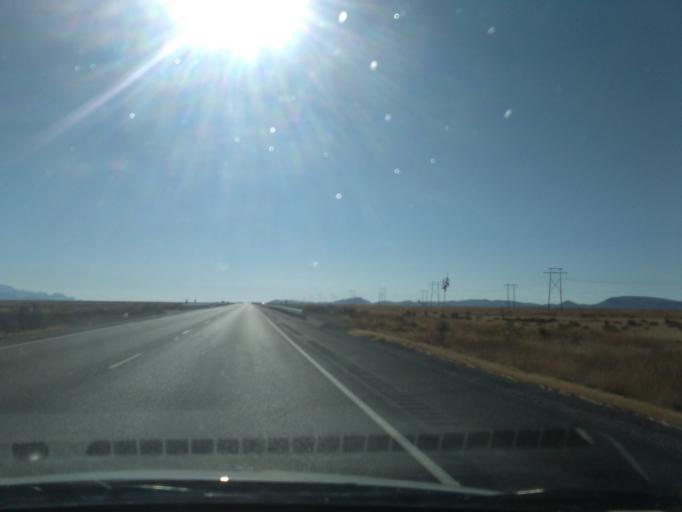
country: US
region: New Mexico
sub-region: Luna County
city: Deming
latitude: 32.4790
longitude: -107.5293
